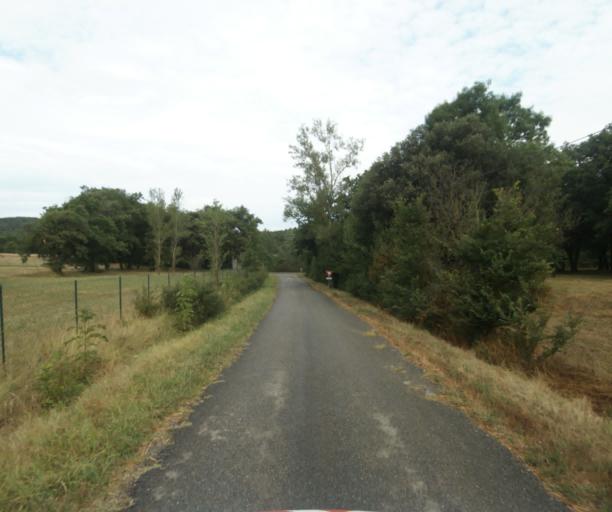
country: FR
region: Midi-Pyrenees
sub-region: Departement de la Haute-Garonne
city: Revel
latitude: 43.4276
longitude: 1.9954
